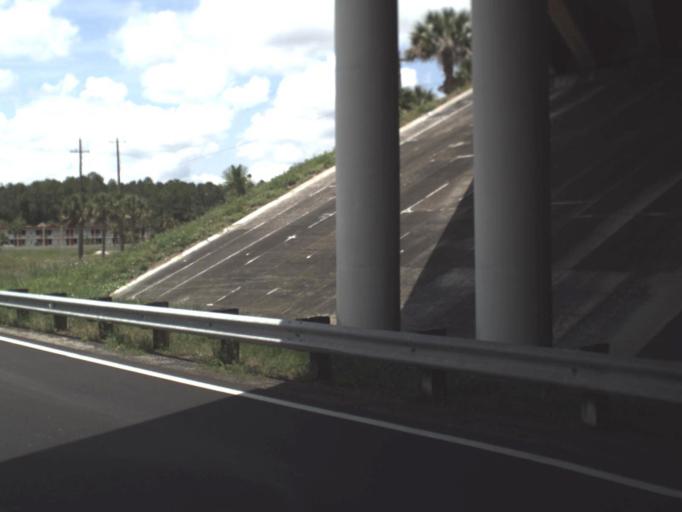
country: US
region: Georgia
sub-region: Camden County
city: Kingsland
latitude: 30.7115
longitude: -81.6716
